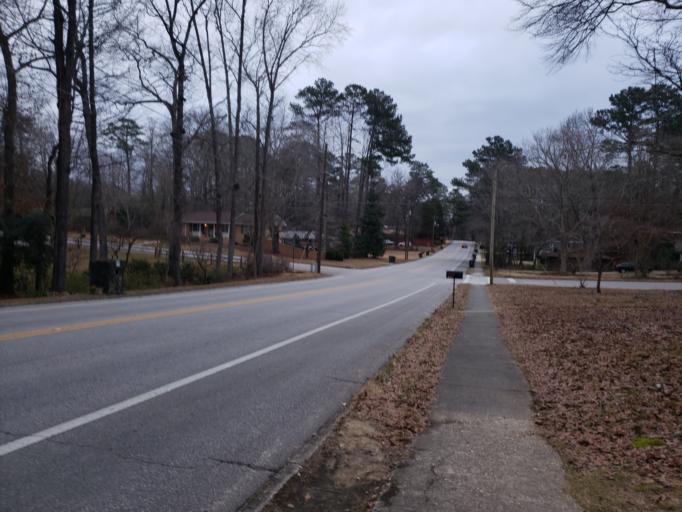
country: US
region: Alabama
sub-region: Lee County
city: Auburn
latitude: 32.5989
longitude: -85.4591
